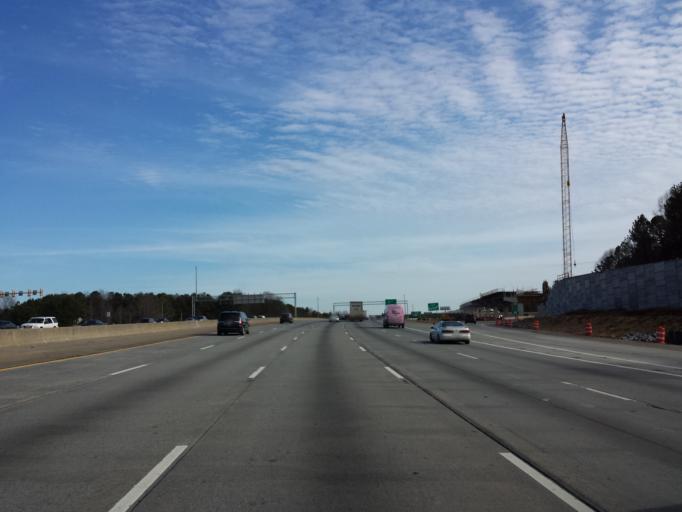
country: US
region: Georgia
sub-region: Cobb County
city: Marietta
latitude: 33.9880
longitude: -84.5459
